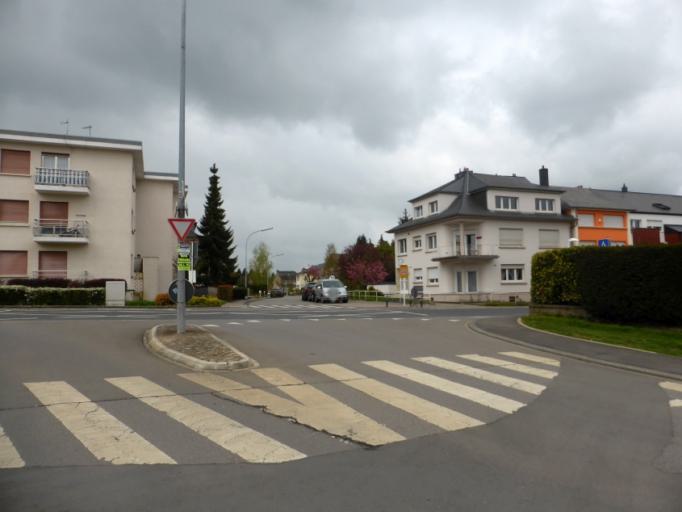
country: LU
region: Luxembourg
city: Bridel
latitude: 49.6599
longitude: 6.0824
